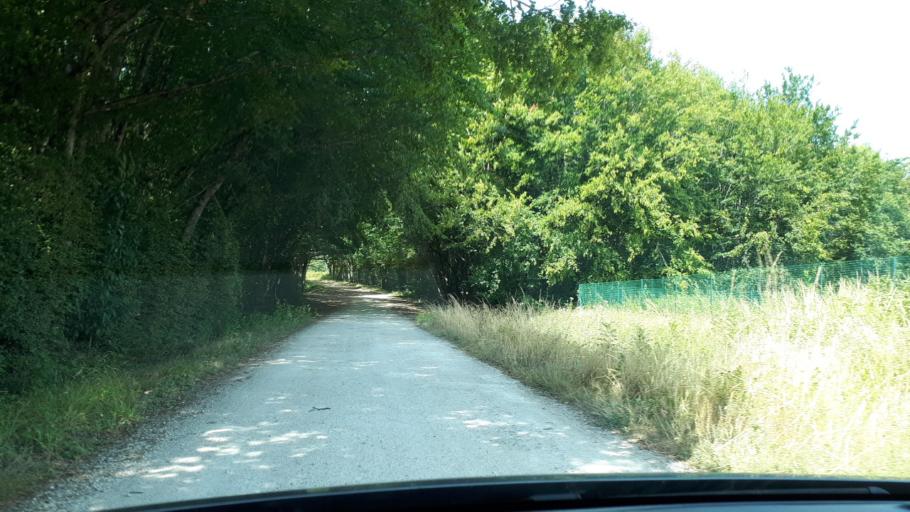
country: FR
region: Centre
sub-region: Departement du Loir-et-Cher
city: Vendome
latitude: 47.8266
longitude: 1.0536
